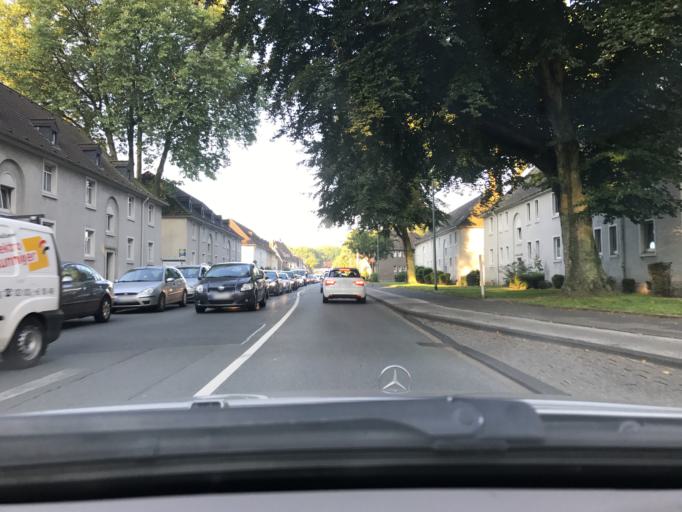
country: DE
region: North Rhine-Westphalia
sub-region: Regierungsbezirk Dusseldorf
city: Hochfeld
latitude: 51.4091
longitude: 6.7274
